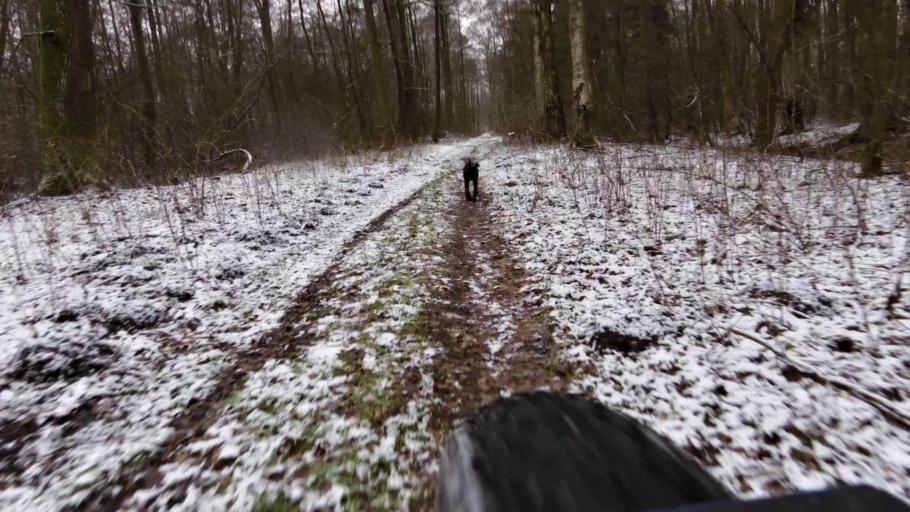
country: PL
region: West Pomeranian Voivodeship
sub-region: Powiat walecki
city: Miroslawiec
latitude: 53.3382
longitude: 16.1058
